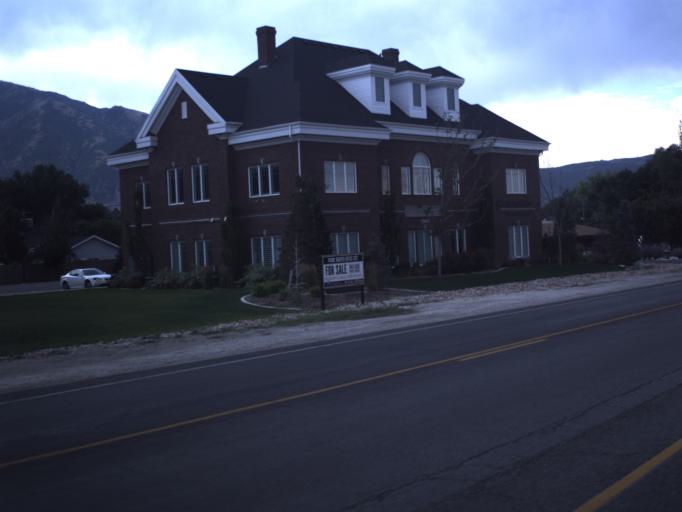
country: US
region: Utah
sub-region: Salt Lake County
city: Draper
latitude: 40.5394
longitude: -111.8713
